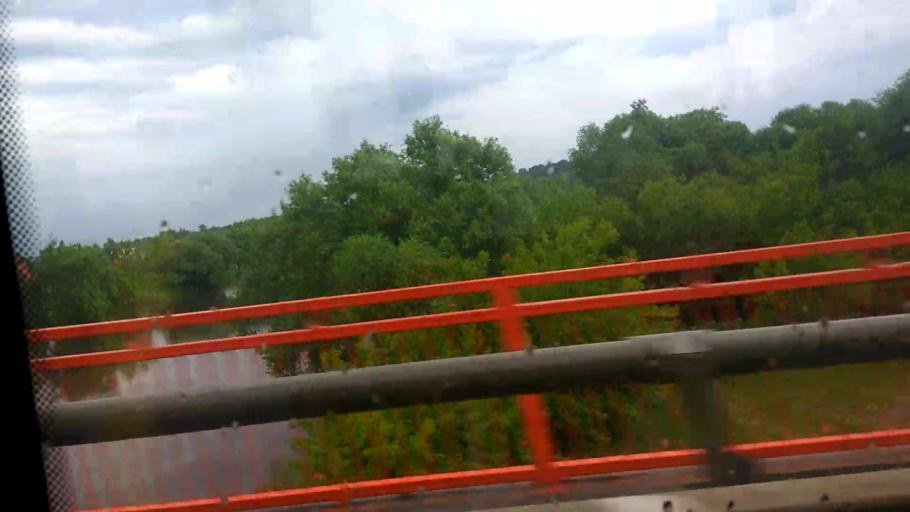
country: RU
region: Moskovskaya
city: Zaraysk
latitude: 54.7560
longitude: 38.8607
